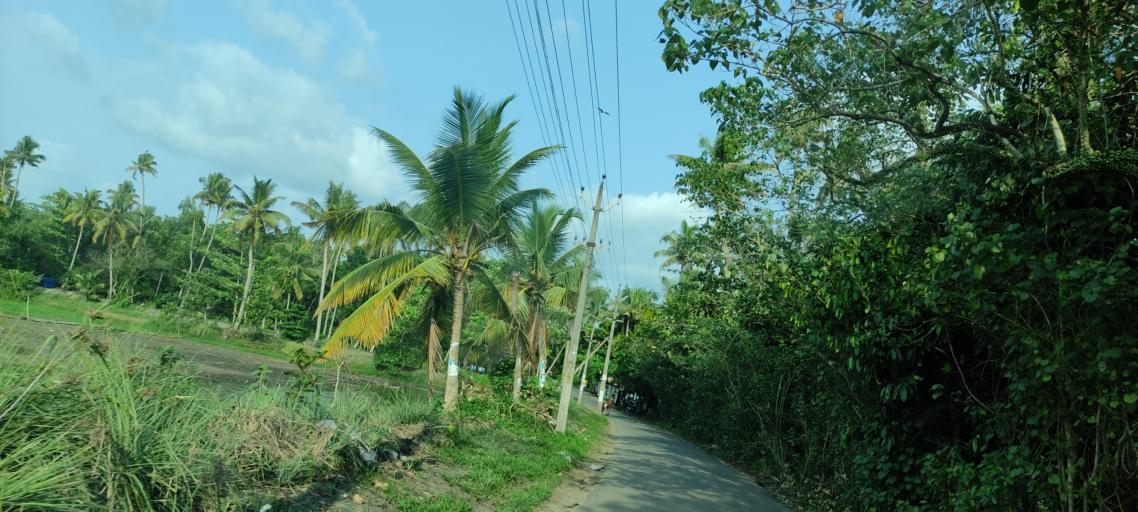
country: IN
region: Kerala
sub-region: Alappuzha
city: Vayalar
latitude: 9.7283
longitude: 76.3034
